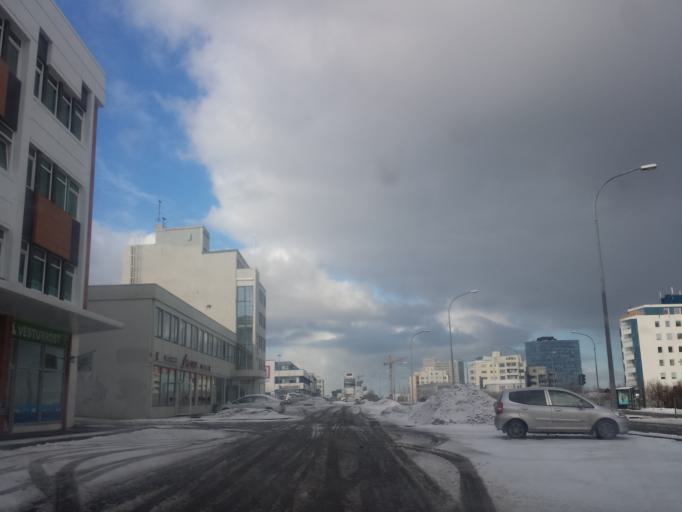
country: IS
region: Capital Region
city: Reykjavik
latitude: 64.1406
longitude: -21.8970
